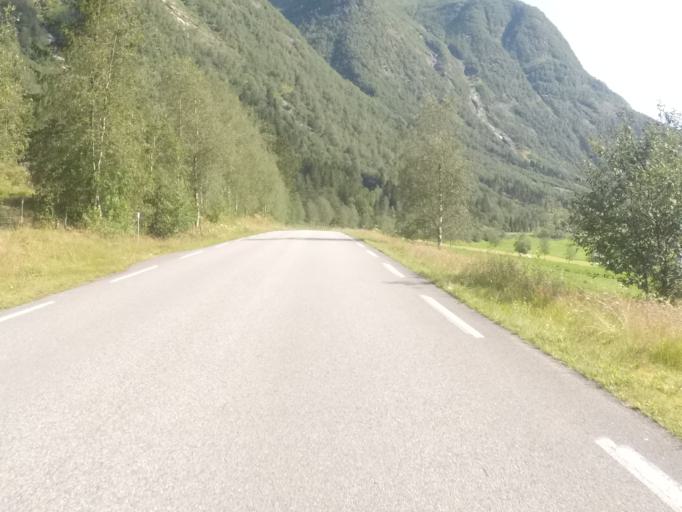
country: NO
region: Sogn og Fjordane
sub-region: Balestrand
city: Balestrand
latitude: 61.3211
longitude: 6.5745
